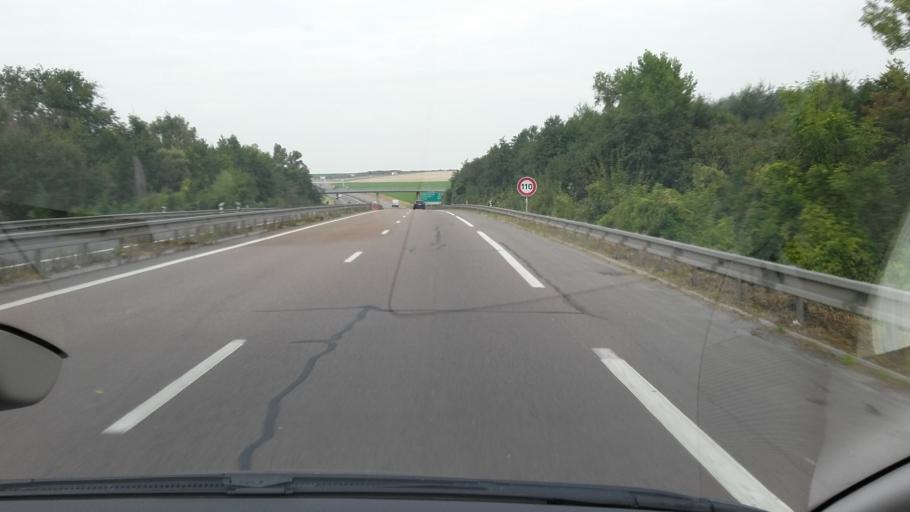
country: FR
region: Champagne-Ardenne
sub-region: Departement de la Marne
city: Warmeriville
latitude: 49.3550
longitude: 4.2062
